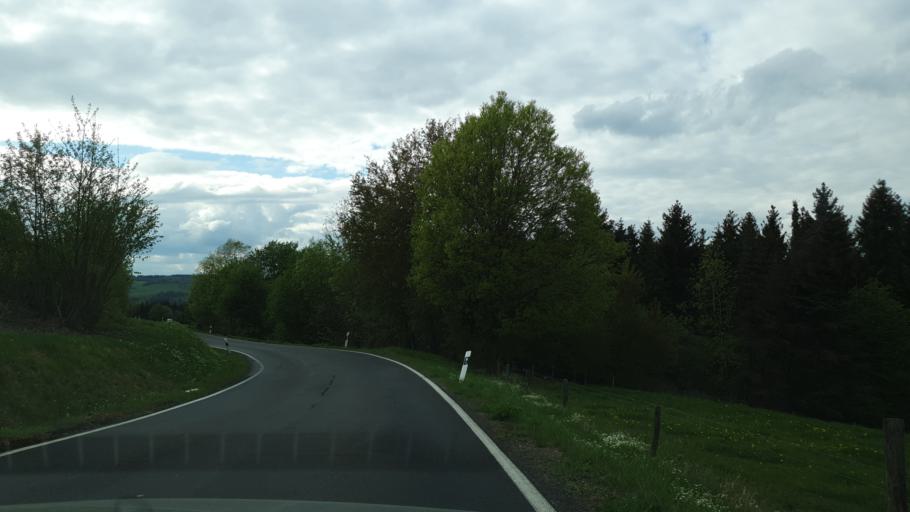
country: DE
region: Rheinland-Pfalz
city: Dreisbach
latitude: 50.6201
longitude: 7.9244
